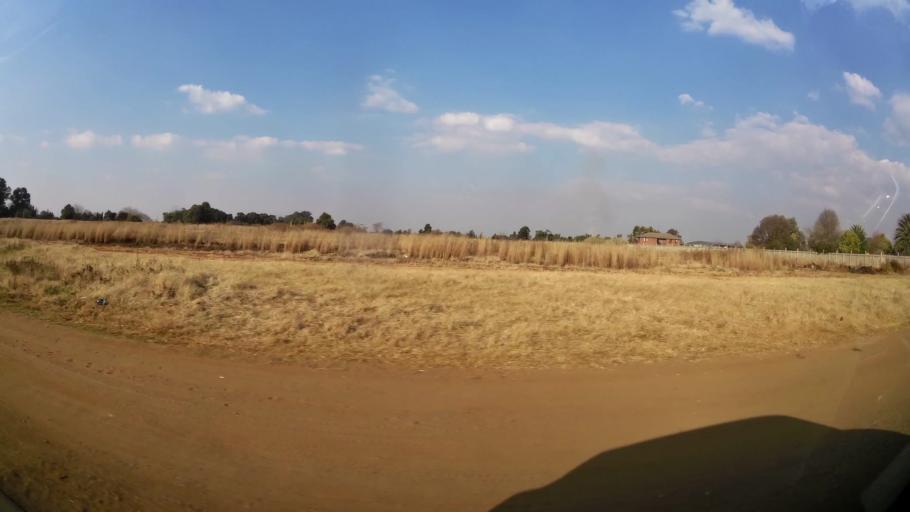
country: ZA
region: Gauteng
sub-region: Ekurhuleni Metropolitan Municipality
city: Benoni
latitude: -26.1063
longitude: 28.2962
